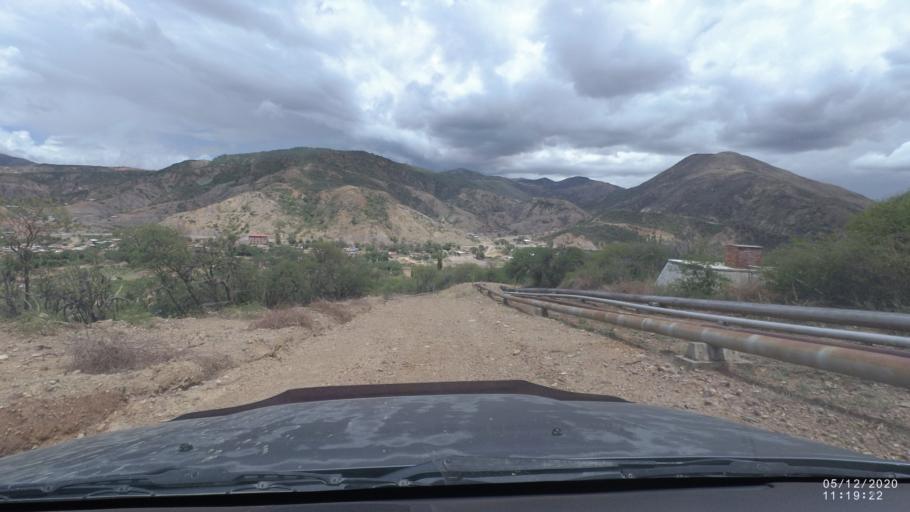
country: BO
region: Cochabamba
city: Sipe Sipe
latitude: -17.5518
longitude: -66.3358
